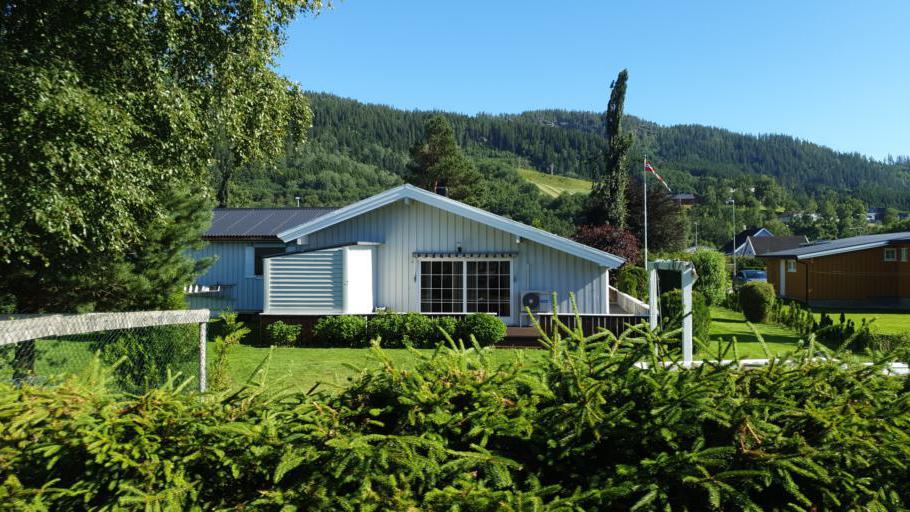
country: NO
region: Sor-Trondelag
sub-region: Orkdal
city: Orkanger
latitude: 63.2804
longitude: 9.8311
